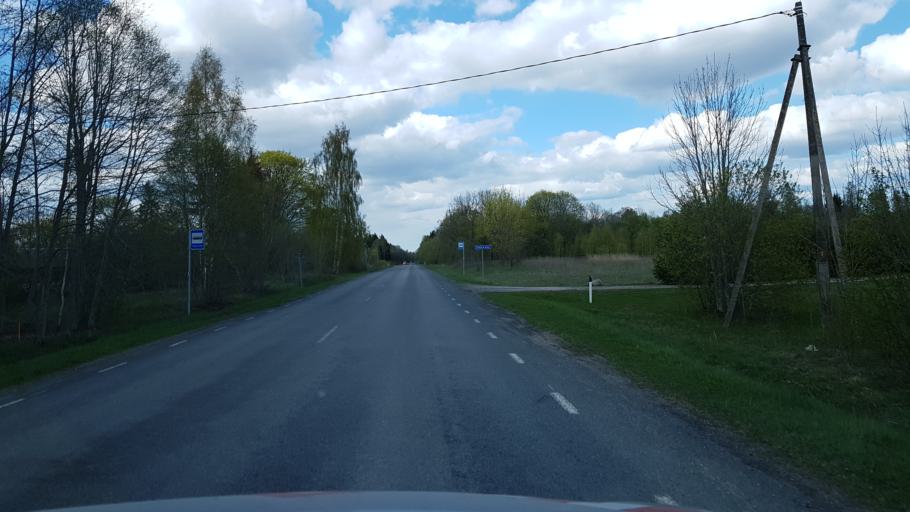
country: EE
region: Harju
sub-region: Keila linn
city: Keila
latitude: 59.2555
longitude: 24.4554
